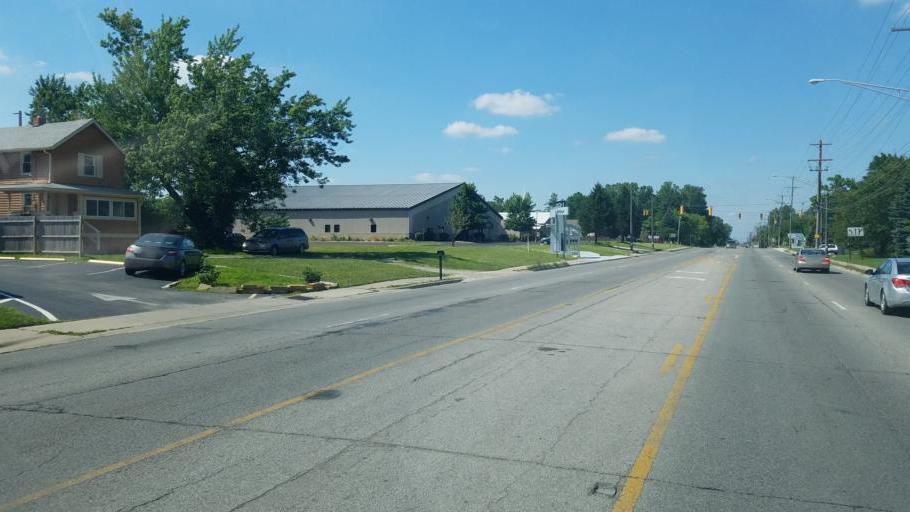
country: US
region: Ohio
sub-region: Franklin County
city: Minerva Park
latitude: 40.0714
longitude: -82.9521
